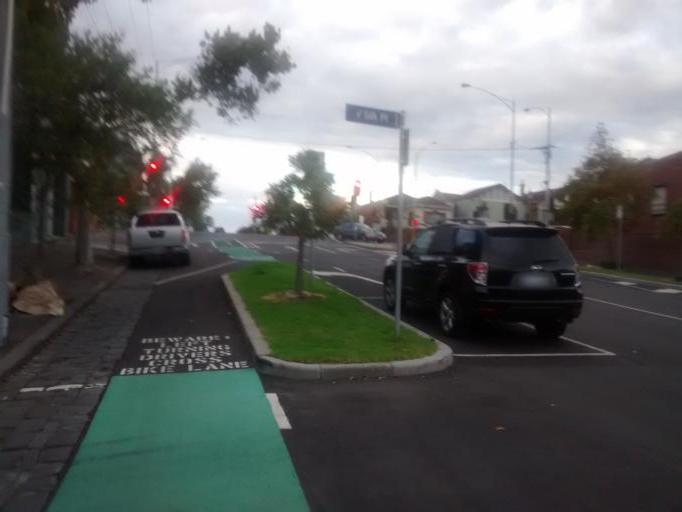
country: AU
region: Victoria
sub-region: Melbourne
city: North Melbourne
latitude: -37.8052
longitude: 144.9450
